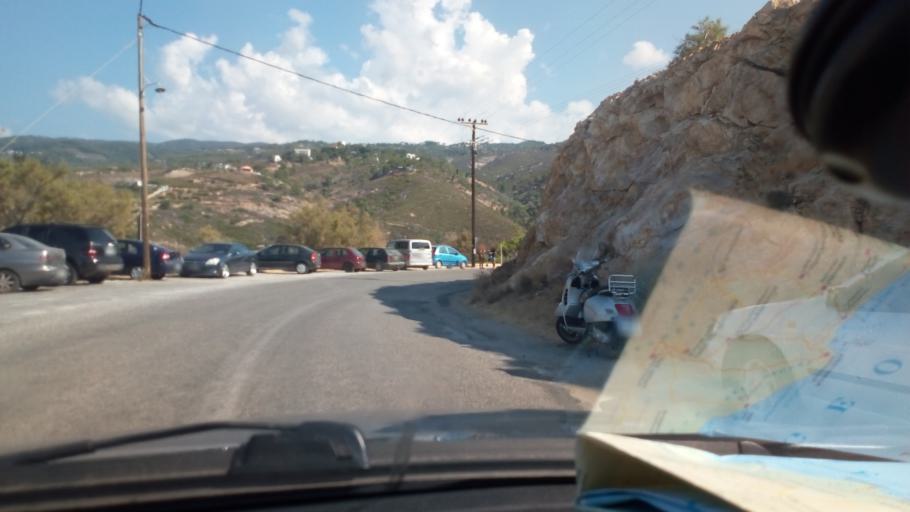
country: GR
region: North Aegean
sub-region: Nomos Samou
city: Agios Kirykos
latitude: 37.6316
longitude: 26.0885
